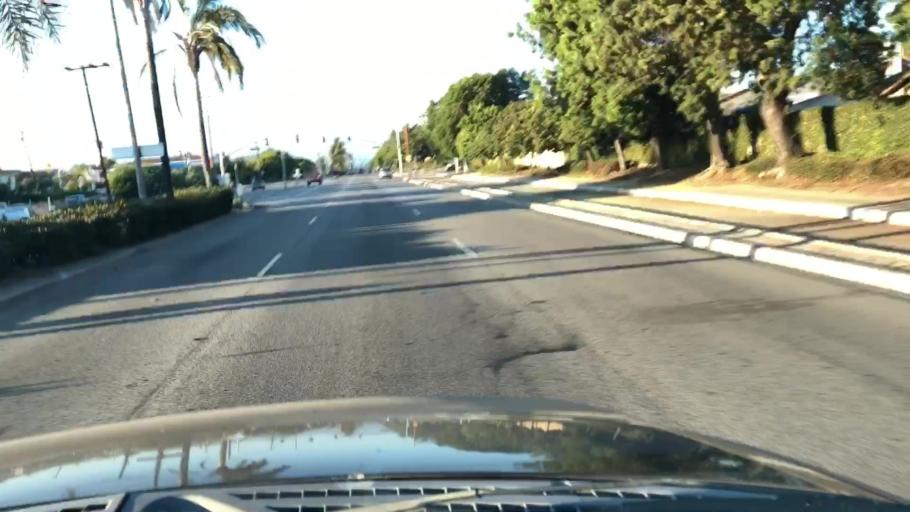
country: US
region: California
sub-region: Ventura County
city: Oxnard
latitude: 34.1912
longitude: -119.1947
